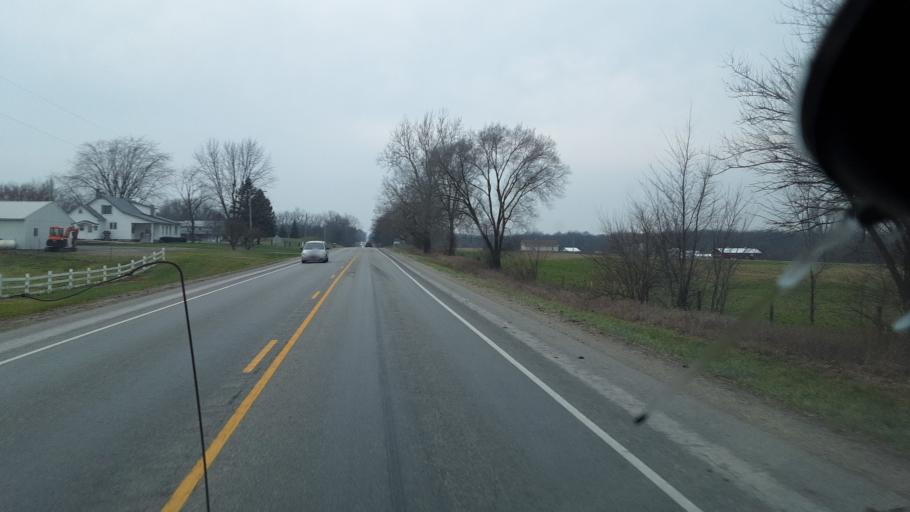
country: US
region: Michigan
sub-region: Saint Joseph County
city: White Pigeon
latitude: 41.7265
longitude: -85.6169
